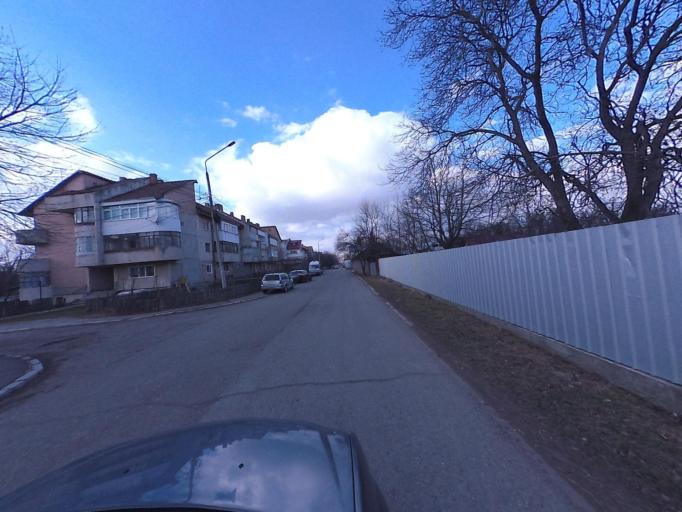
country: RO
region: Neamt
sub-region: Oras Targu Neamt
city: Targu Neamt
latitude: 47.2018
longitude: 26.3769
